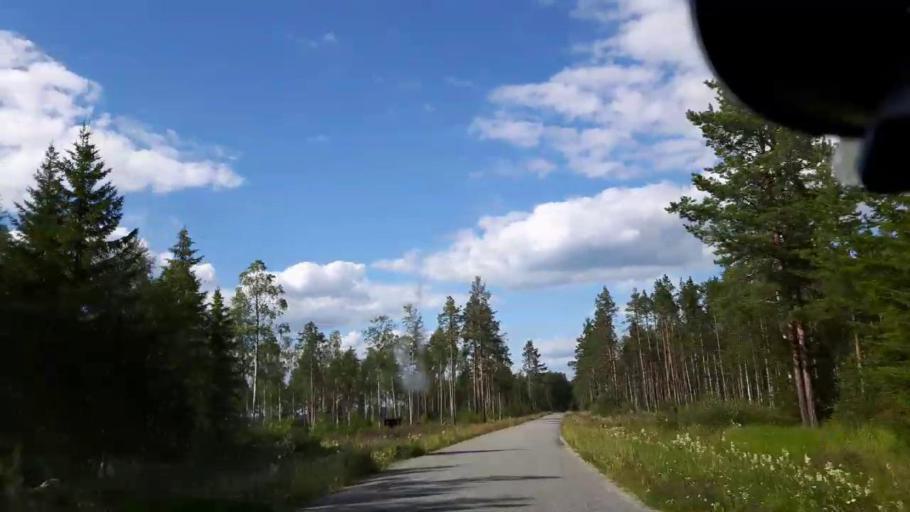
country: SE
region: Jaemtland
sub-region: Braecke Kommun
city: Braecke
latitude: 62.8431
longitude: 15.2975
